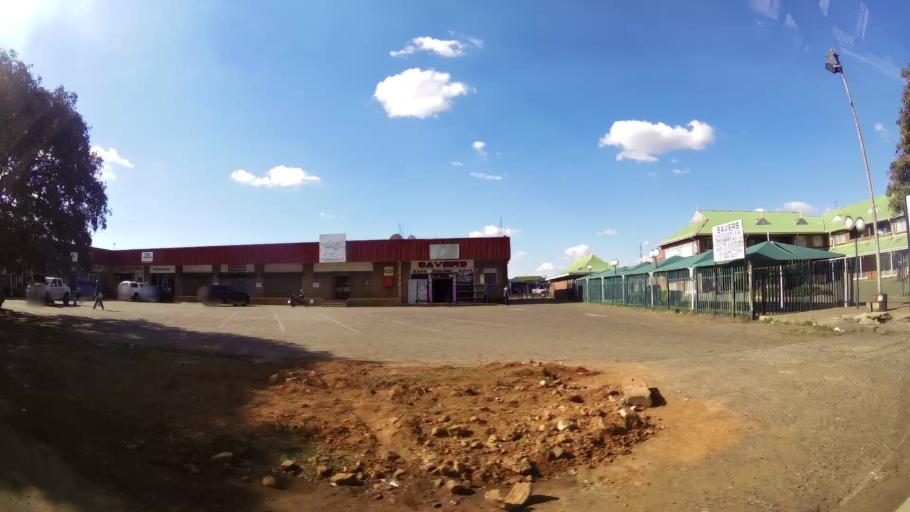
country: ZA
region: Mpumalanga
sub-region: Nkangala District Municipality
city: Witbank
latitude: -25.9018
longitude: 29.2310
